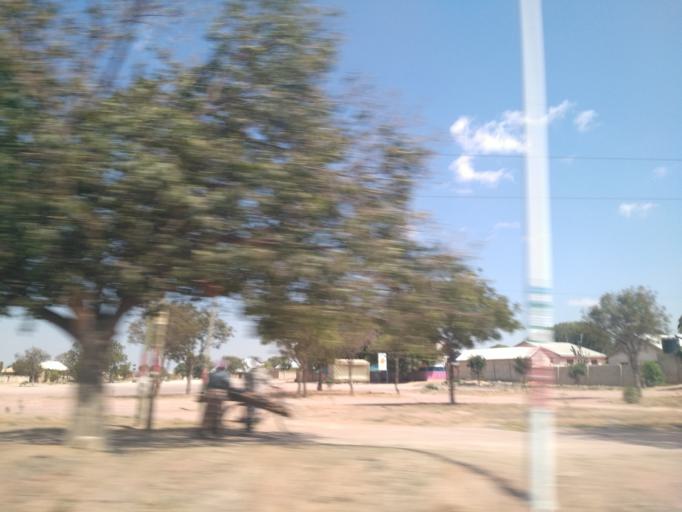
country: TZ
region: Dodoma
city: Dodoma
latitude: -6.1557
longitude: 35.7229
